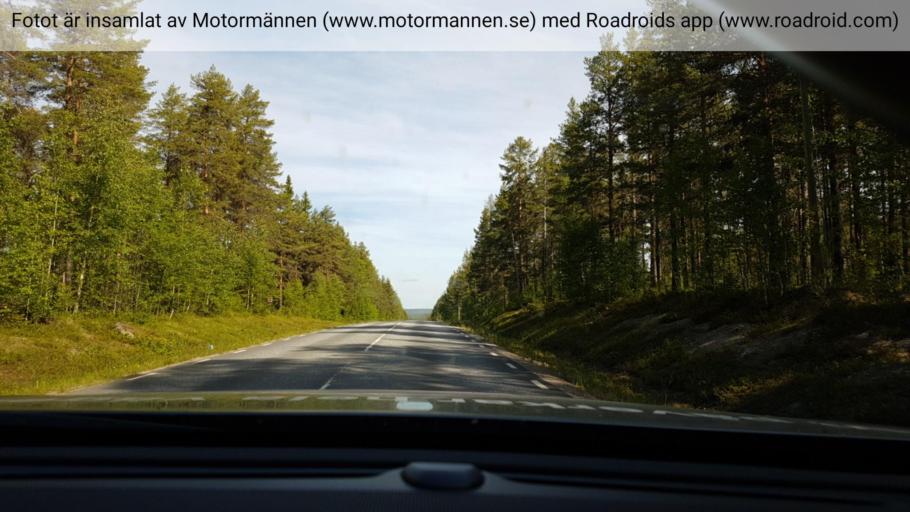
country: SE
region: Vaesterbotten
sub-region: Dorotea Kommun
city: Dorotea
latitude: 64.2726
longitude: 16.3462
